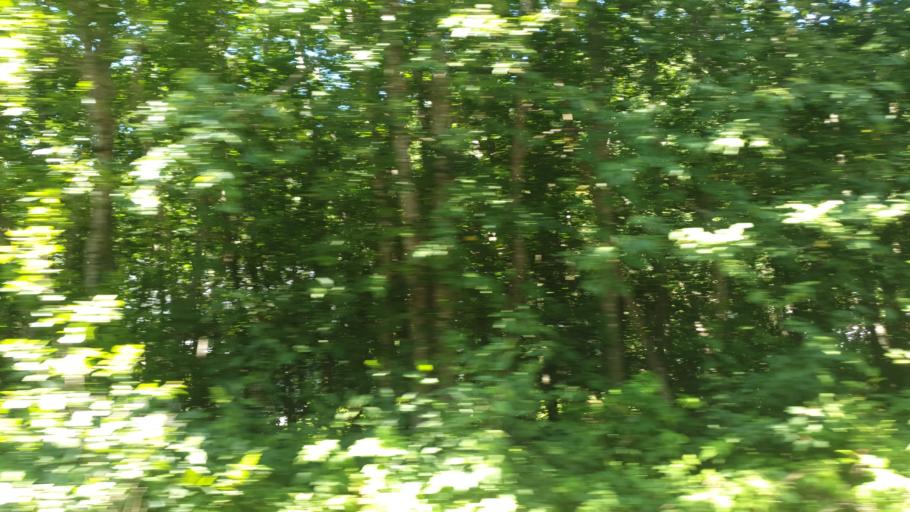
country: NO
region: Sor-Trondelag
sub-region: Meldal
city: Meldal
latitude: 63.1417
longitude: 9.7116
